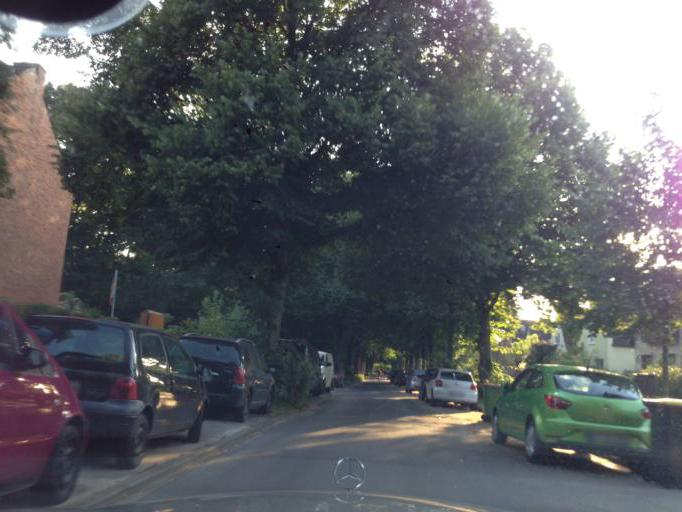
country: DE
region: Hamburg
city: Wandsbek
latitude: 53.5688
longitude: 10.1204
